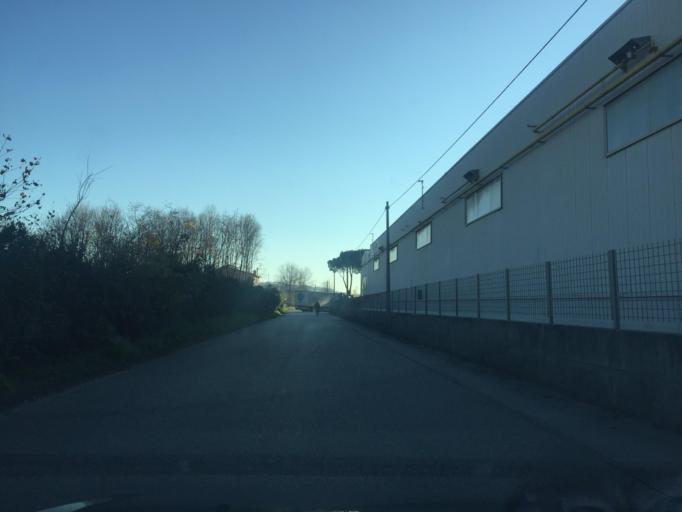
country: IT
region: Friuli Venezia Giulia
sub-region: Provincia di Udine
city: Osoppo
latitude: 46.2505
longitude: 13.1096
